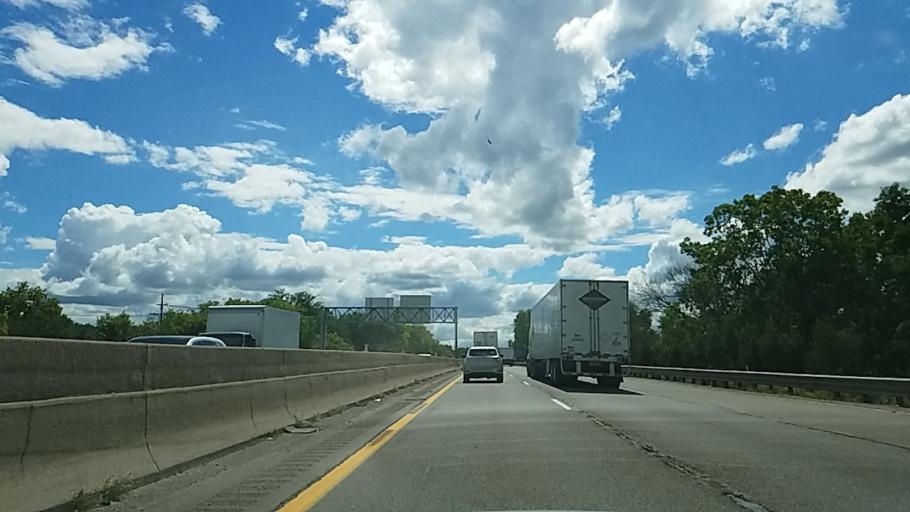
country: US
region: Michigan
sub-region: Livingston County
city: Whitmore Lake
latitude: 42.4421
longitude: -83.7547
